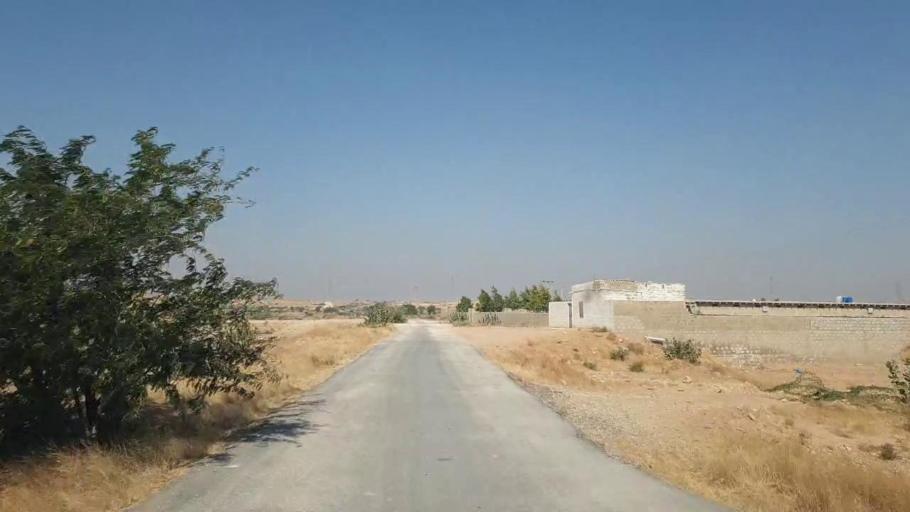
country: PK
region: Sindh
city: Thatta
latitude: 25.1890
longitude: 67.8037
